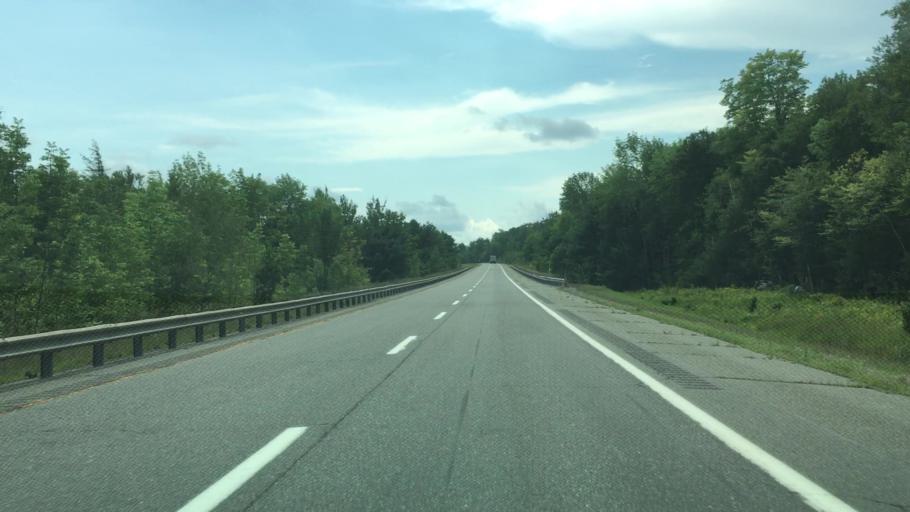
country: US
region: Maine
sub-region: Penobscot County
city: Lincoln
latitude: 45.4642
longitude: -68.5861
